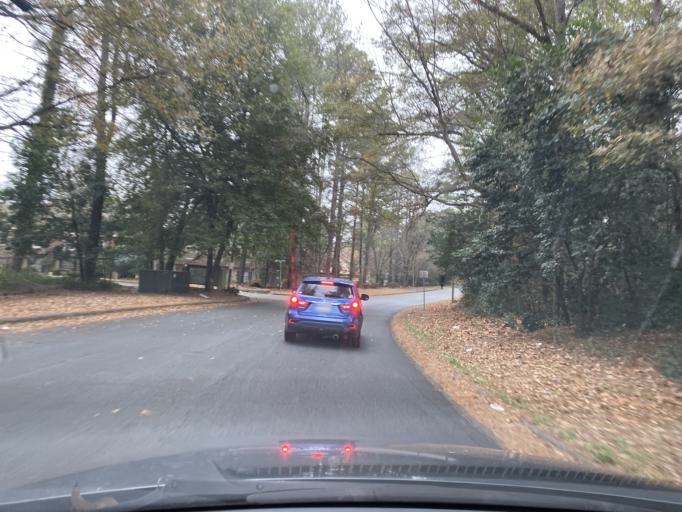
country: US
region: Georgia
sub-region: DeKalb County
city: Pine Mountain
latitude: 33.6994
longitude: -84.1467
